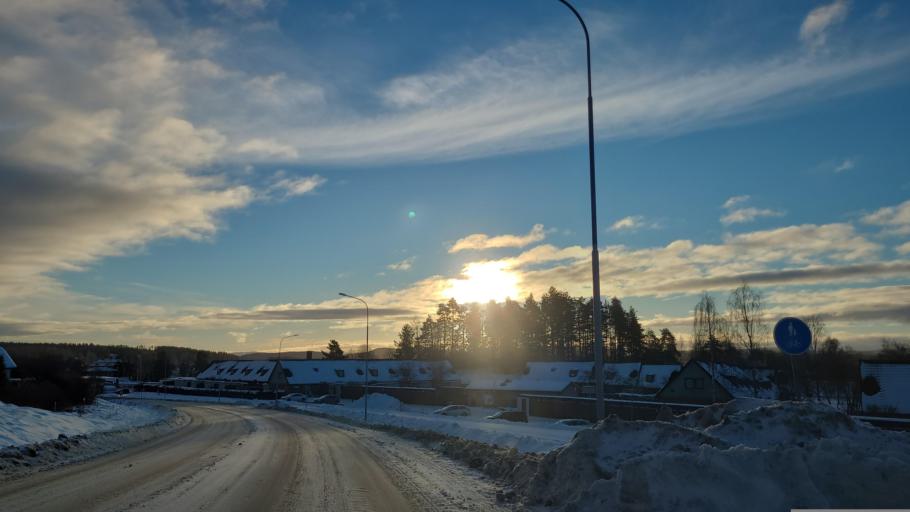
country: SE
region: Gaevleborg
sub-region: Bollnas Kommun
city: Bollnas
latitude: 61.3588
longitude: 16.4204
